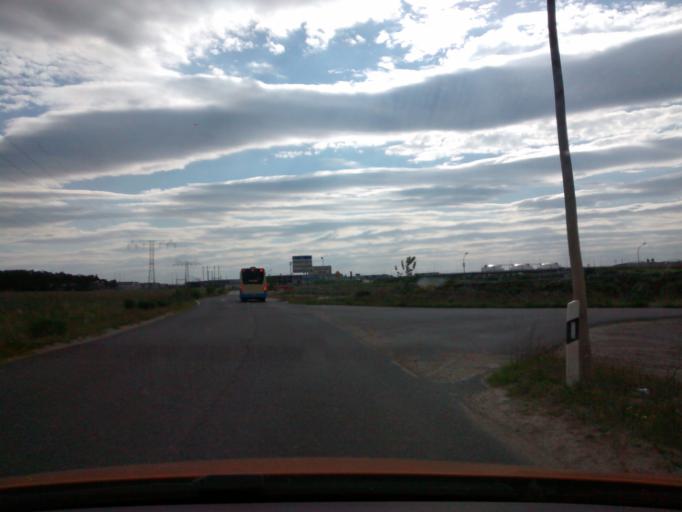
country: DE
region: Brandenburg
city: Schonefeld
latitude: 52.3695
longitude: 13.5422
